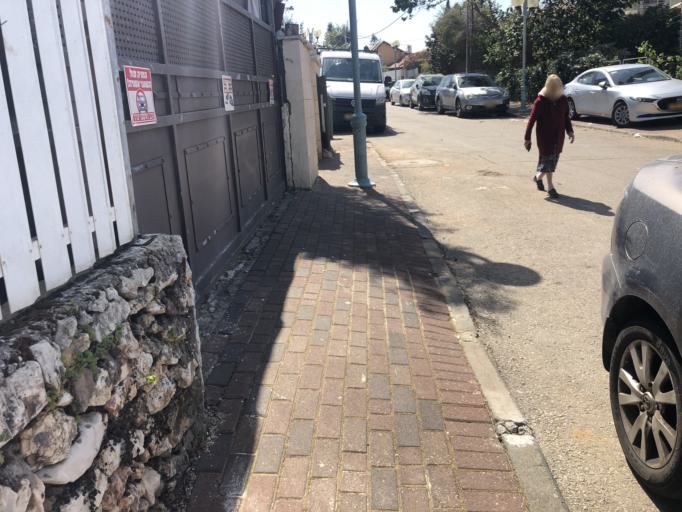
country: IL
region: Central District
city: Kfar Saba
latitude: 32.1612
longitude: 34.9220
